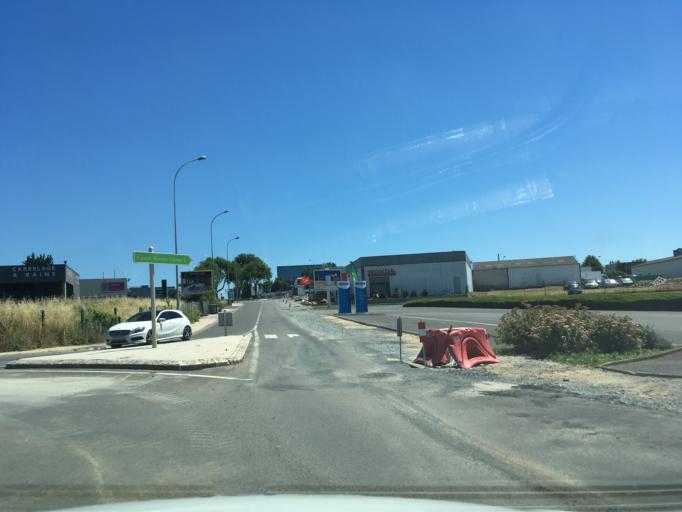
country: FR
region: Poitou-Charentes
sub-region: Departement des Deux-Sevres
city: Aiffres
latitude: 46.3347
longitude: -0.4162
